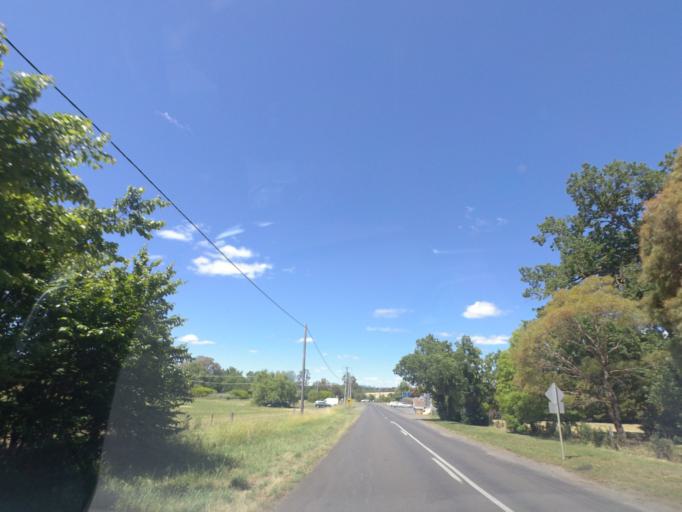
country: AU
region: Victoria
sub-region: Mount Alexander
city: Castlemaine
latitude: -37.2378
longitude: 144.4179
